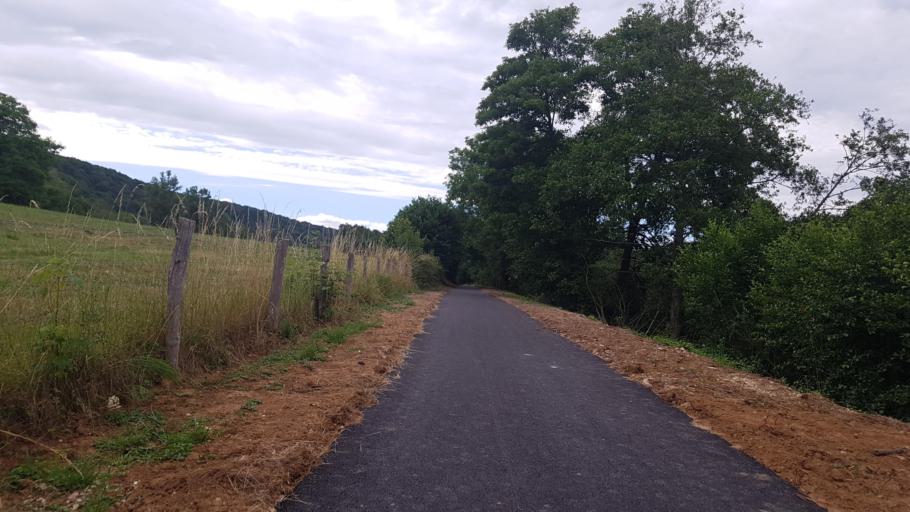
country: FR
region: Lorraine
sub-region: Departement de Meurthe-et-Moselle
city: Chaligny
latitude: 48.6256
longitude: 6.0472
